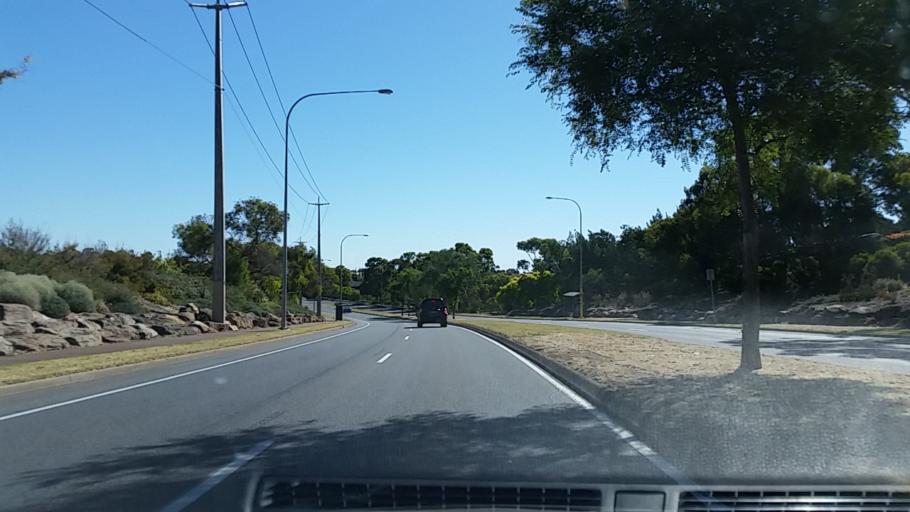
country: AU
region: South Australia
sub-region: Tea Tree Gully
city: Modbury
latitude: -34.8073
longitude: 138.6787
